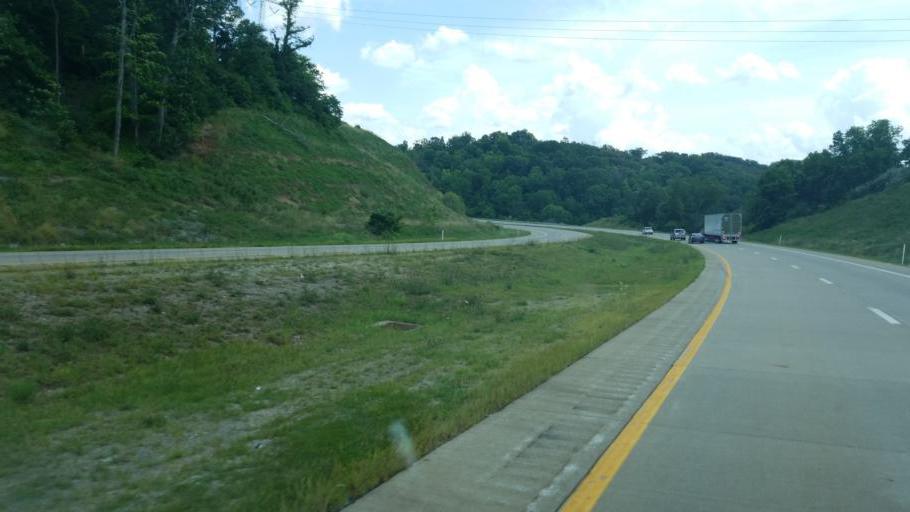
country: US
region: West Virginia
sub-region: Mason County
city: Point Pleasant
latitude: 38.7715
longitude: -82.0540
